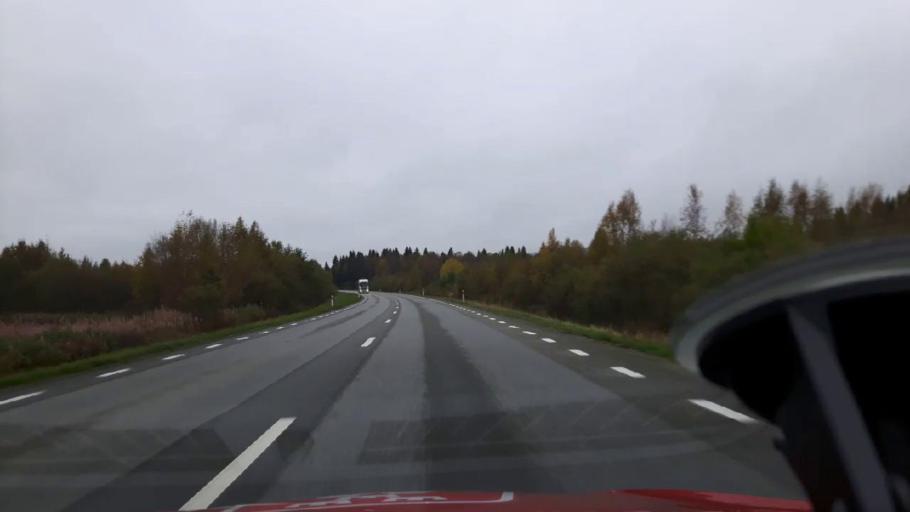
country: SE
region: Jaemtland
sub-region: Bergs Kommun
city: Hoverberg
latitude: 62.7338
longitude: 14.4152
